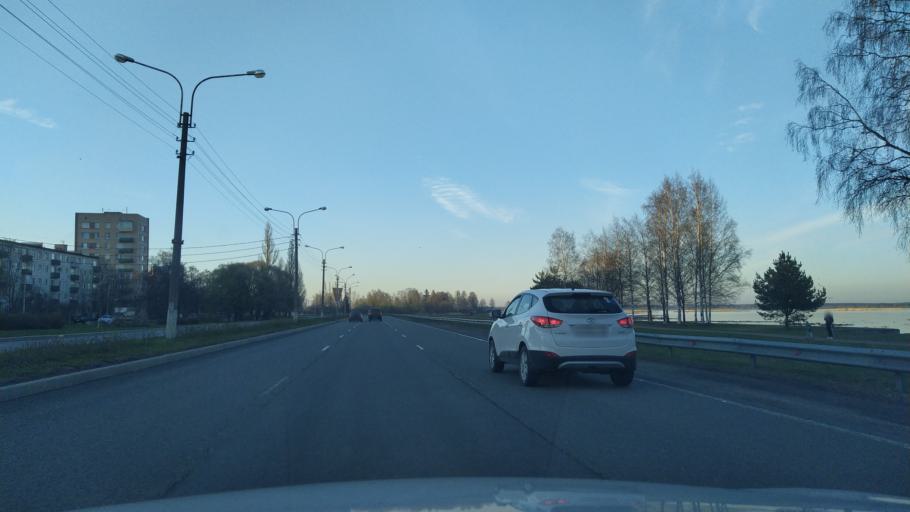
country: RU
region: St.-Petersburg
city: Sestroretsk
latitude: 60.0945
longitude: 29.9777
